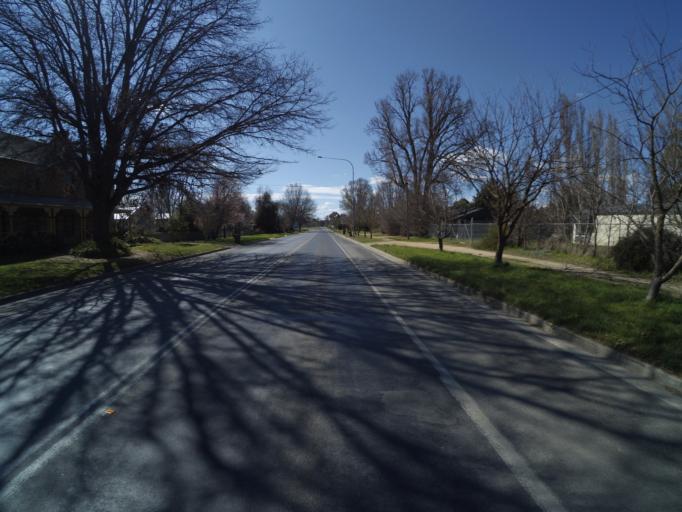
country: AU
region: New South Wales
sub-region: Palerang
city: Bungendore
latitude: -35.2556
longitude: 149.4380
